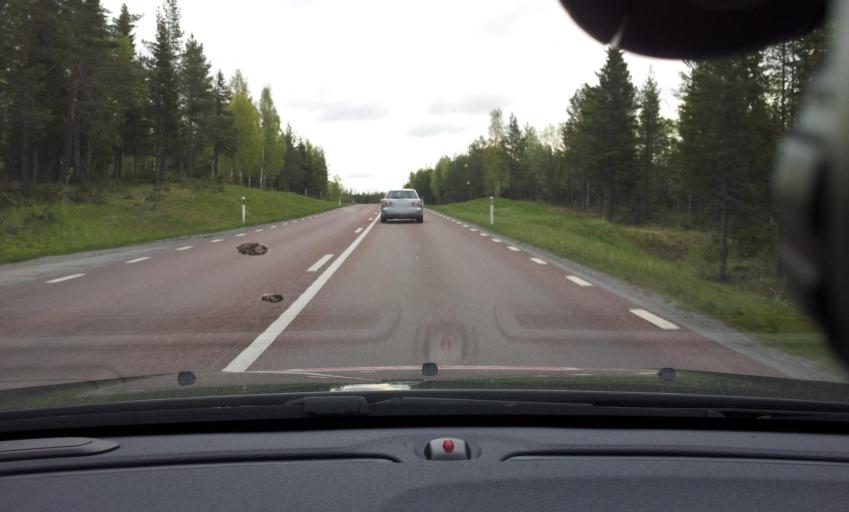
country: SE
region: Jaemtland
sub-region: OEstersunds Kommun
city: Ostersund
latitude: 63.0032
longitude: 14.6626
